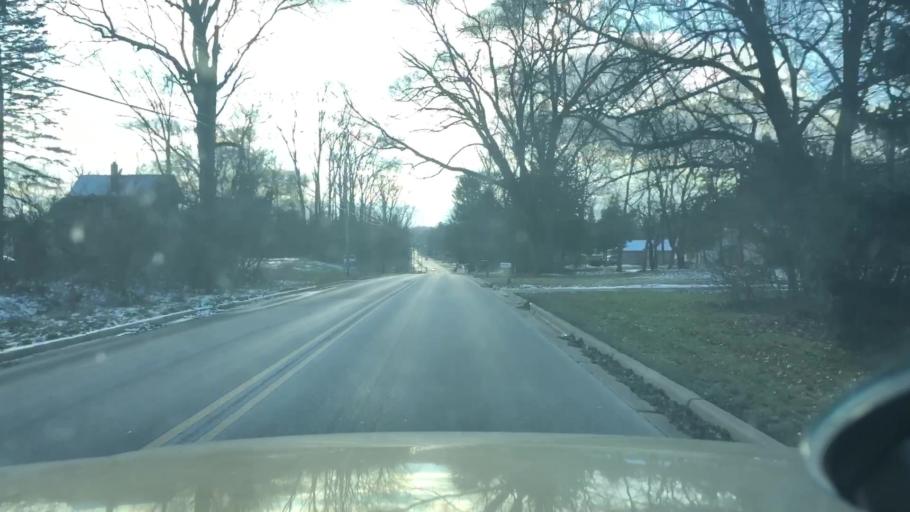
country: US
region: Michigan
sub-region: Jackson County
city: Vandercook Lake
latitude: 42.2102
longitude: -84.4253
